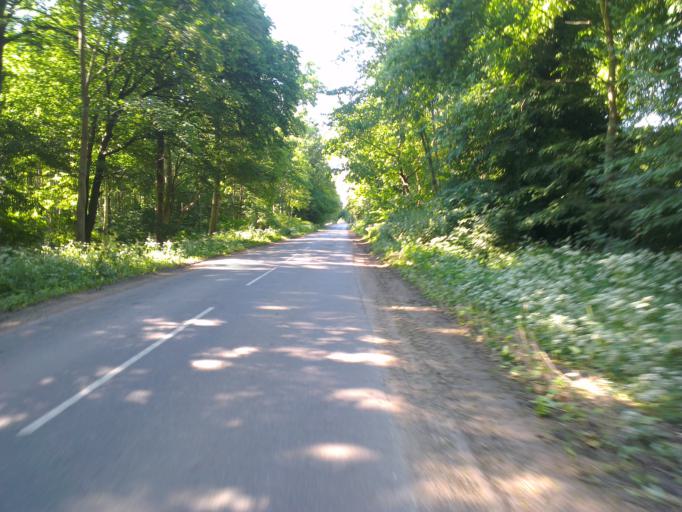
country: DK
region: Capital Region
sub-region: Frederikssund Kommune
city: Skibby
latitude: 55.7851
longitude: 11.9431
